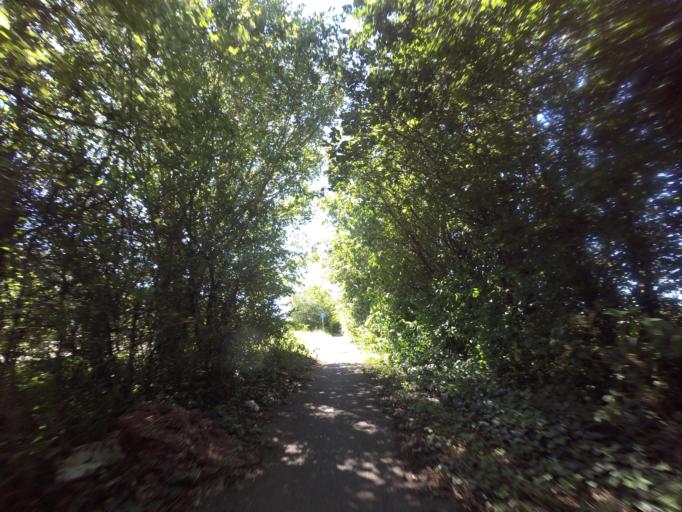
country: GB
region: England
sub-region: Kent
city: Eastry
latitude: 51.2286
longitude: 1.3028
